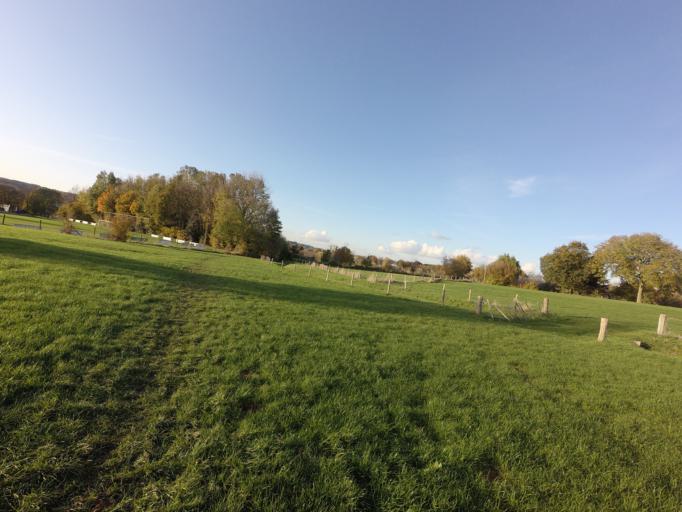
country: BE
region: Wallonia
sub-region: Province de Liege
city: Plombieres
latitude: 50.7924
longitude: 5.9326
